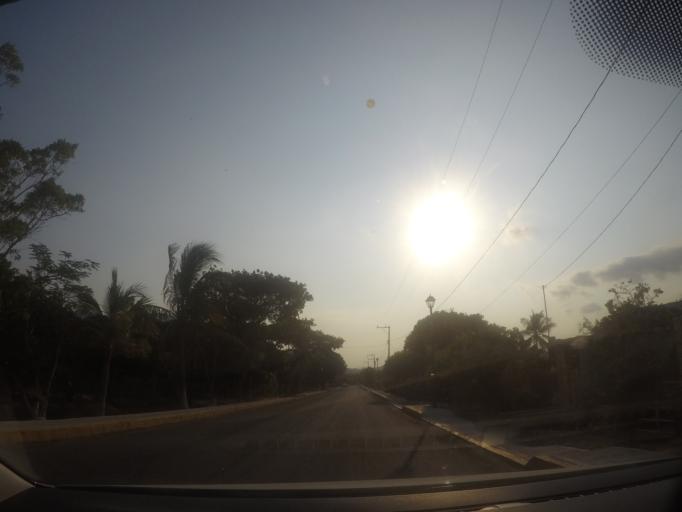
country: MX
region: Oaxaca
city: San Jeronimo Ixtepec
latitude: 16.5822
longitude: -95.1951
